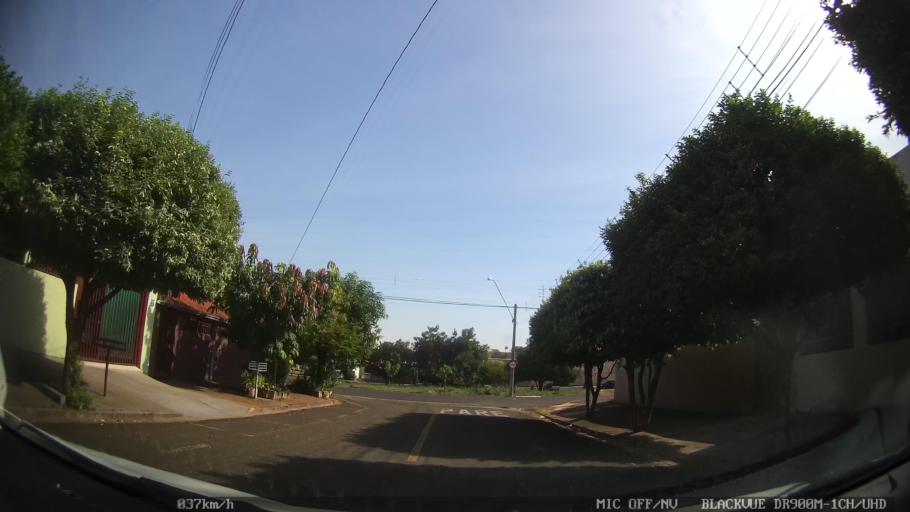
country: BR
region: Sao Paulo
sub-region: Sao Jose Do Rio Preto
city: Sao Jose do Rio Preto
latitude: -20.7990
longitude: -49.4165
